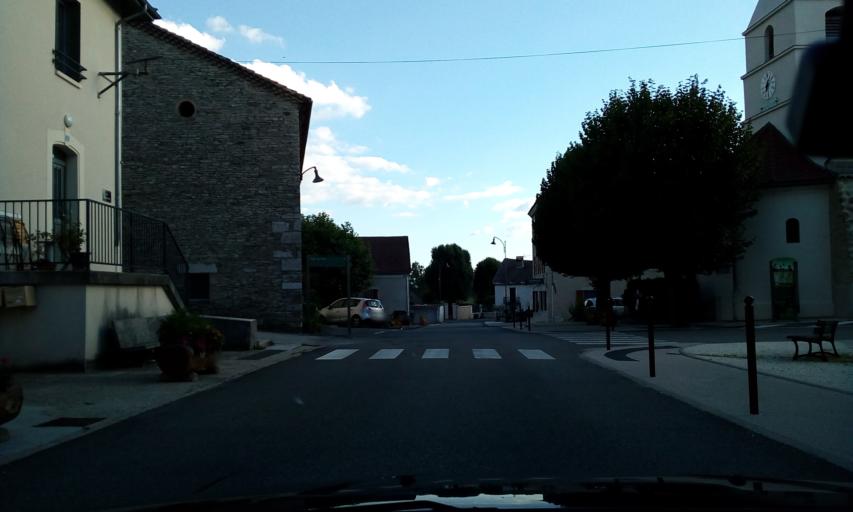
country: FR
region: Rhone-Alpes
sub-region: Departement de l'Isere
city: Villard-de-Lans
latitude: 45.0503
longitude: 5.4491
